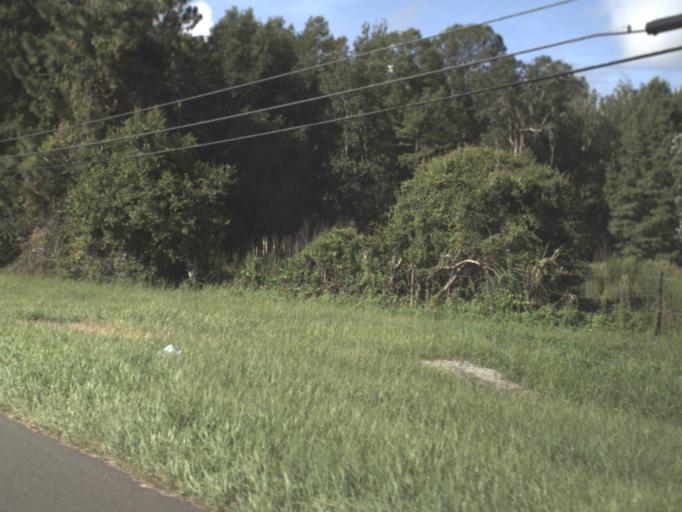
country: US
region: Florida
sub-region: Pasco County
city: Shady Hills
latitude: 28.3518
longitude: -82.5045
